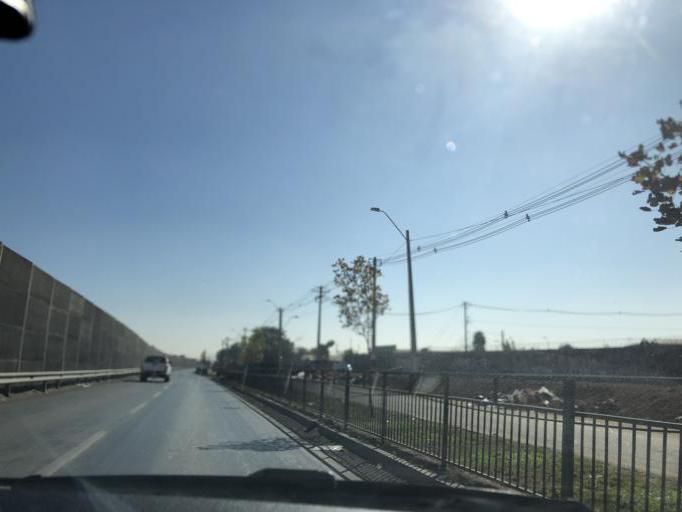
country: CL
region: Santiago Metropolitan
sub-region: Provincia de Cordillera
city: Puente Alto
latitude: -33.6141
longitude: -70.6005
